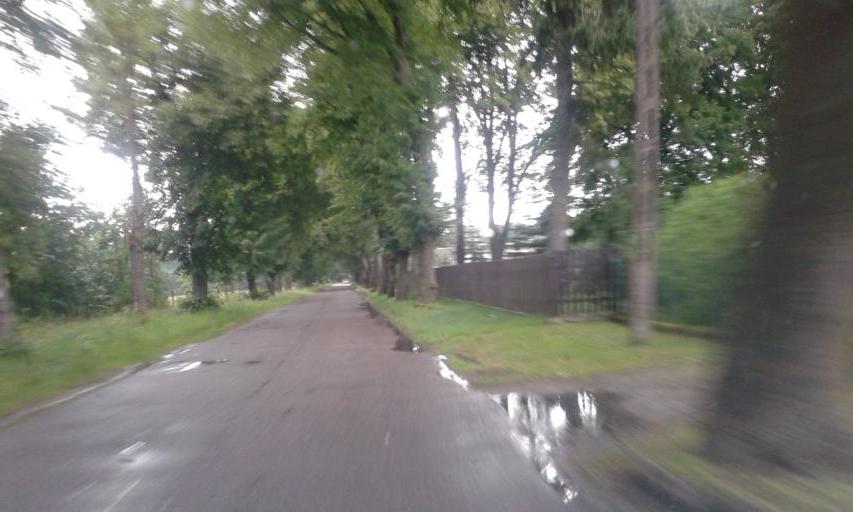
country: PL
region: Greater Poland Voivodeship
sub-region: Powiat zlotowski
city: Sypniewo
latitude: 53.4692
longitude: 16.4967
